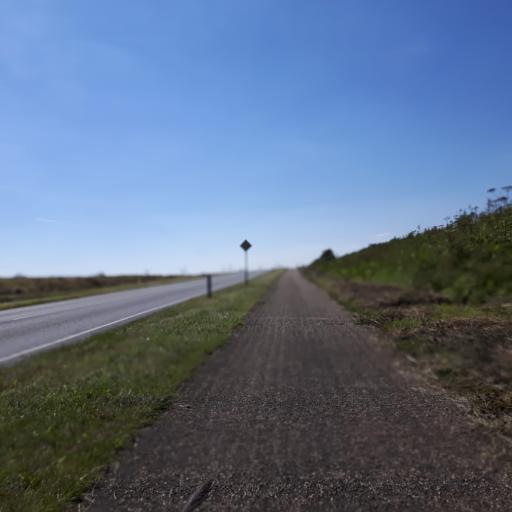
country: NL
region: North Brabant
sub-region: Gemeente Woensdrecht
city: Woensdrecht
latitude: 51.4451
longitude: 4.2941
